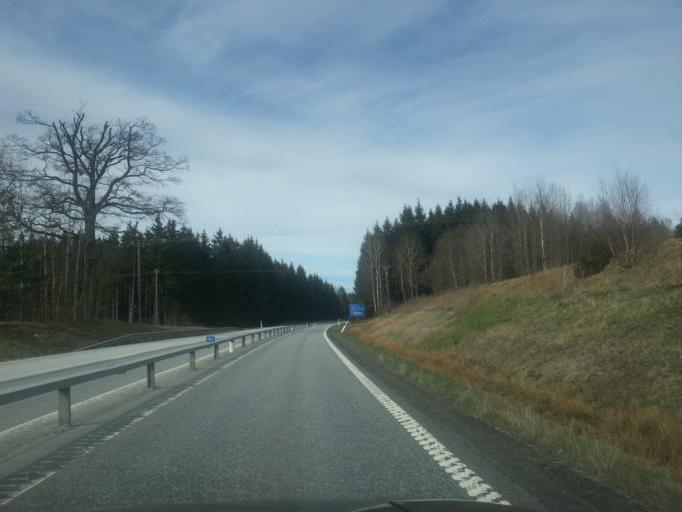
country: SE
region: Joenkoeping
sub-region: Jonkopings Kommun
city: Bankeryd
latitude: 57.8477
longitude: 14.1053
